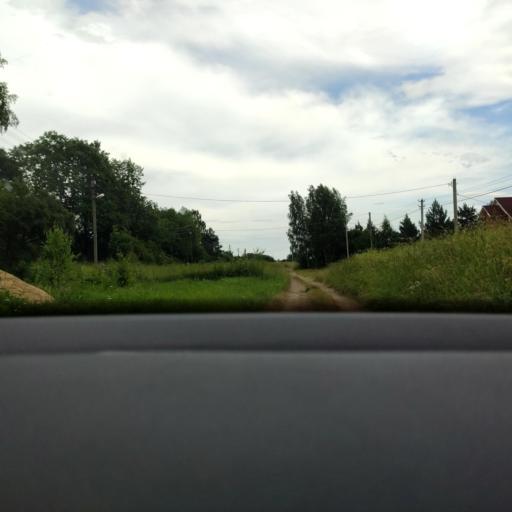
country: RU
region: Moskovskaya
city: Dedenevo
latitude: 56.2565
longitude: 37.5677
